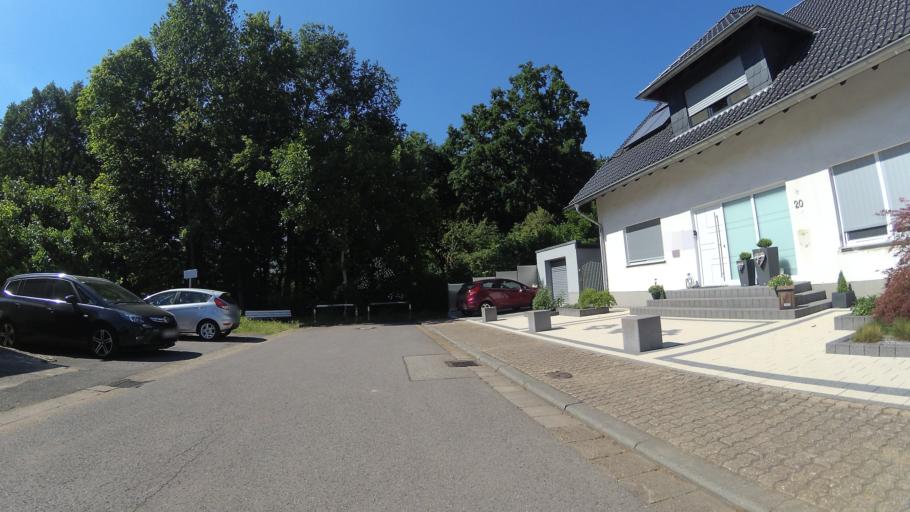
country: DE
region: Saarland
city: Saarwellingen
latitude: 49.3486
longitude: 6.7953
